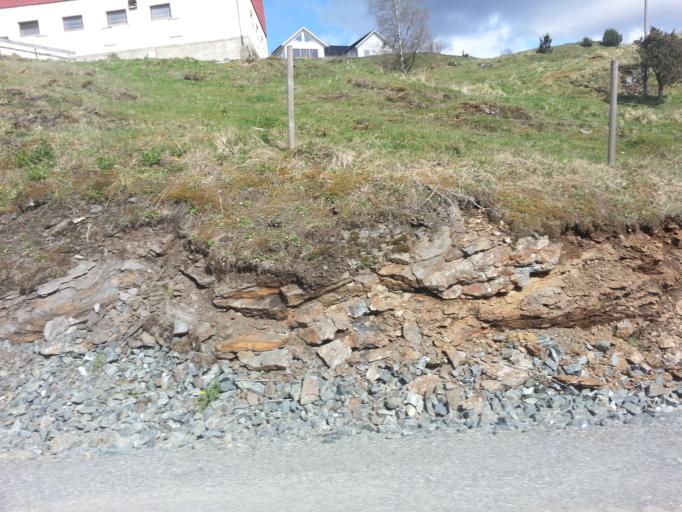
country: NO
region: Nord-Trondelag
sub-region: Levanger
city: Skogn
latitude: 63.6352
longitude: 11.2743
